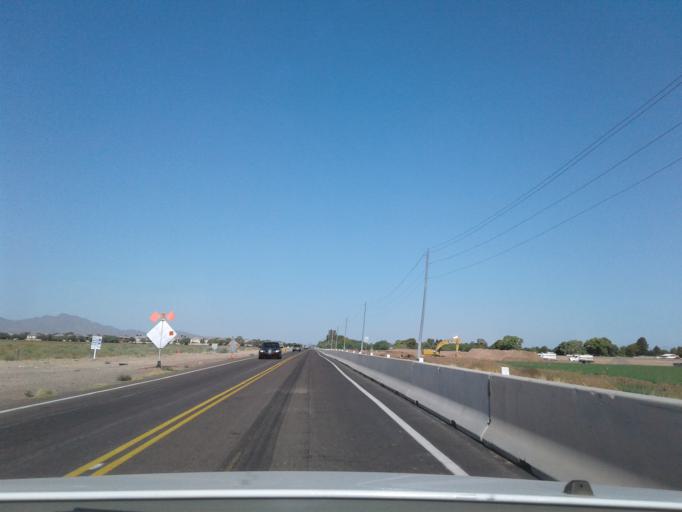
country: US
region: Arizona
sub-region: Maricopa County
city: Laveen
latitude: 33.3774
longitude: -112.1871
